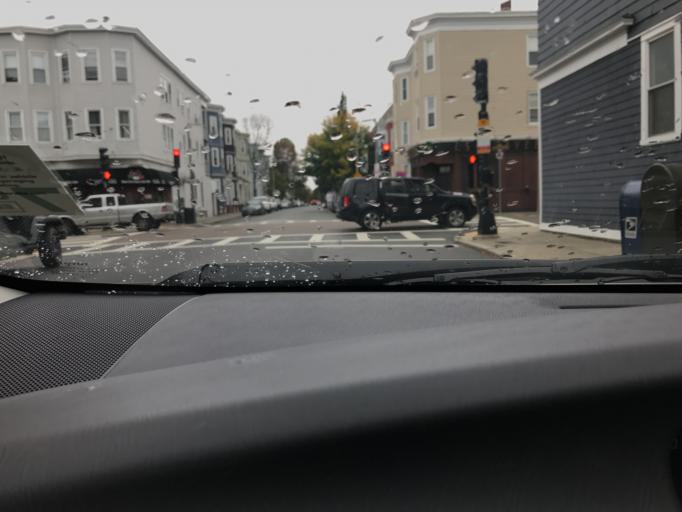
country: US
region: Massachusetts
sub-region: Suffolk County
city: South Boston
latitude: 42.3315
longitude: -71.0350
